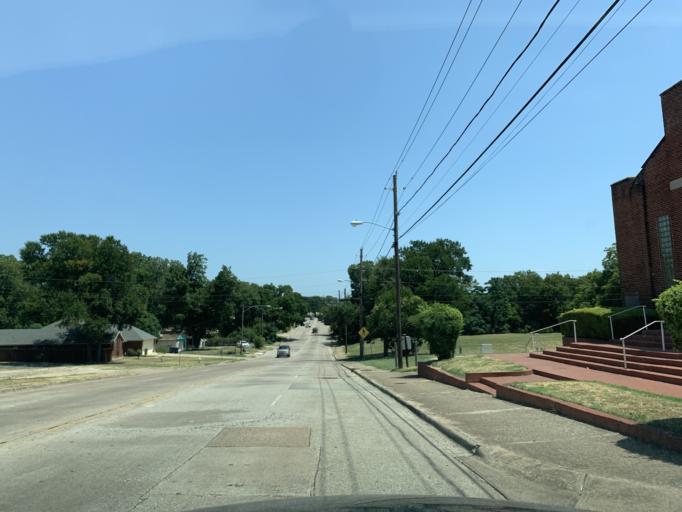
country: US
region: Texas
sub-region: Dallas County
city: Dallas
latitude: 32.6950
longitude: -96.7991
